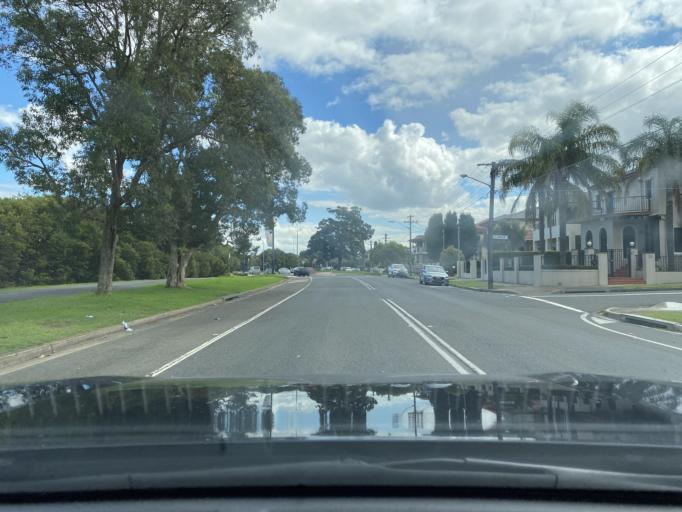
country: AU
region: New South Wales
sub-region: Canada Bay
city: Wareemba
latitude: -33.8679
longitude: 151.1427
